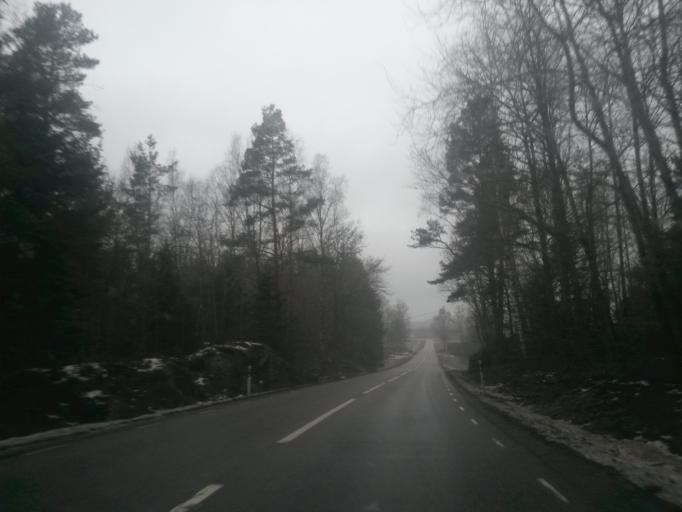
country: SE
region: Vaestra Goetaland
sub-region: Alingsas Kommun
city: Sollebrunn
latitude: 58.1140
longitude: 12.5616
